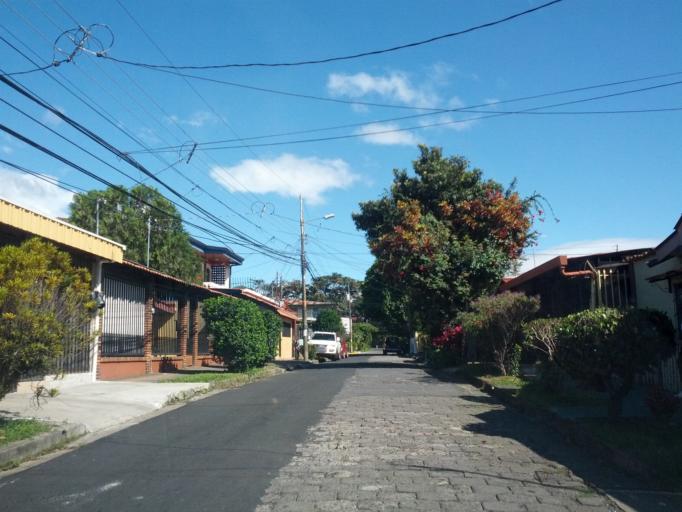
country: CR
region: Alajuela
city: Alajuela
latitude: 10.0233
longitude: -84.2064
